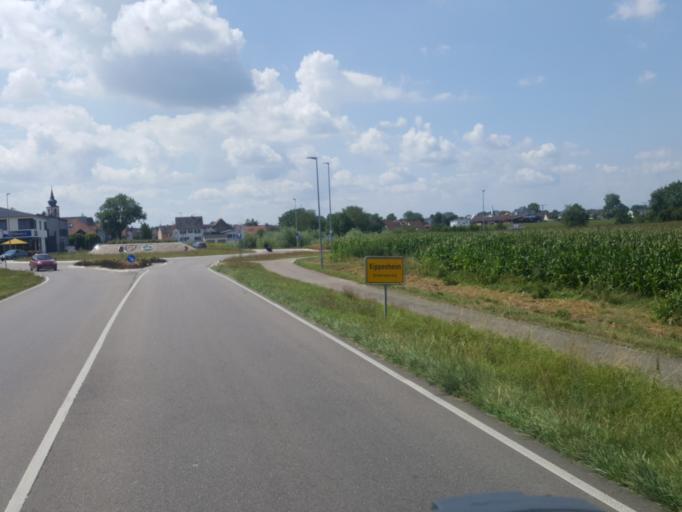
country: DE
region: Baden-Wuerttemberg
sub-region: Freiburg Region
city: Kippenheim
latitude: 48.3006
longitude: 7.8278
